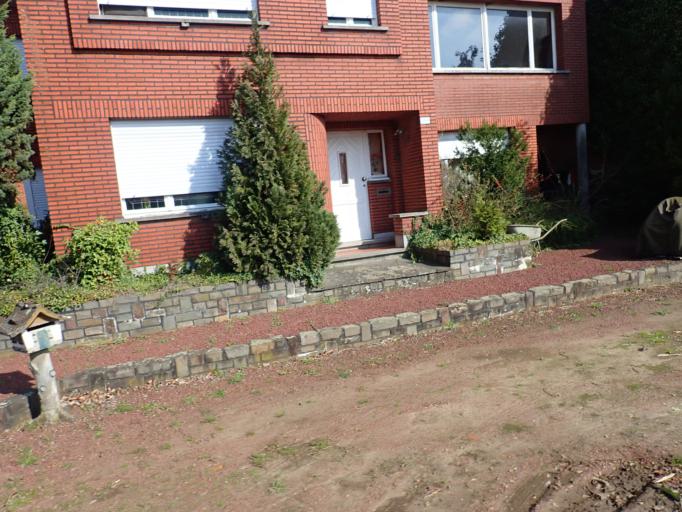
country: BE
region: Flanders
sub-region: Provincie Antwerpen
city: Hulshout
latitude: 51.0706
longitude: 4.8207
